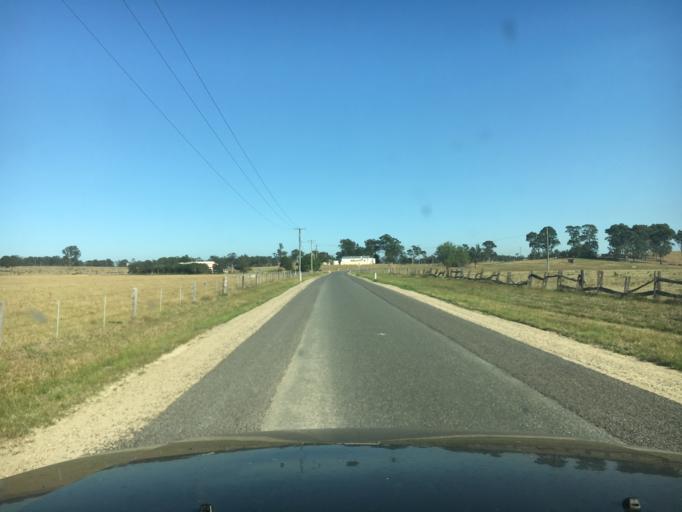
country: AU
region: New South Wales
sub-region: Singleton
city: Singleton
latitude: -32.5575
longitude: 151.2842
